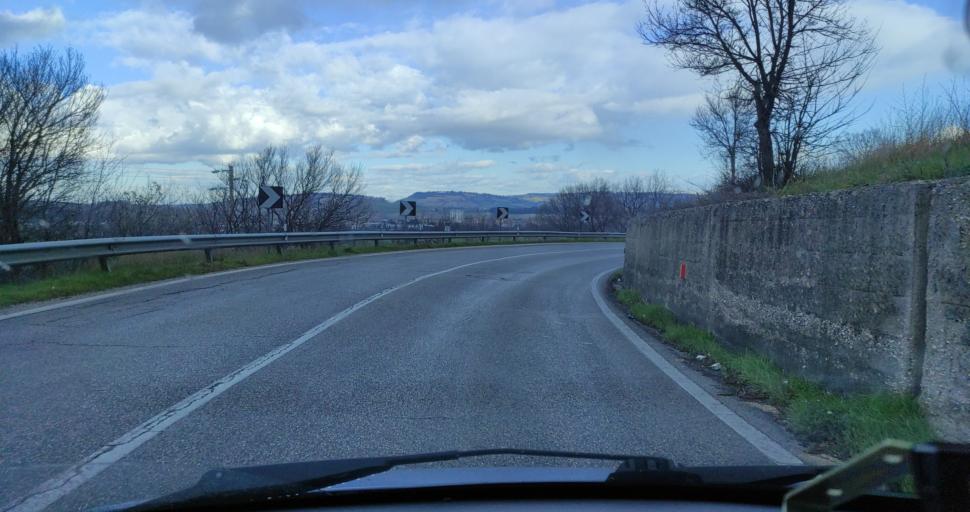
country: IT
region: The Marches
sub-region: Provincia di Macerata
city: Casette Verdini
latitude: 43.2342
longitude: 13.4059
